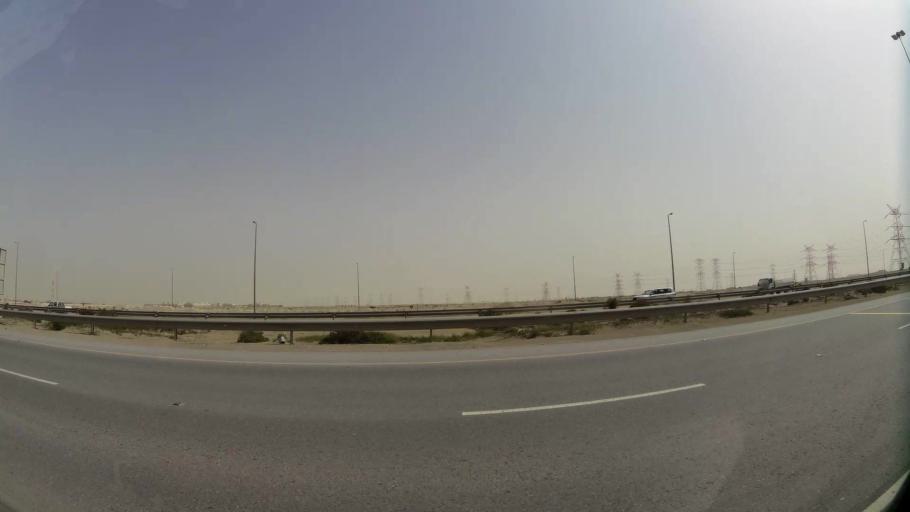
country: QA
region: Baladiyat ar Rayyan
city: Ar Rayyan
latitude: 25.1764
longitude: 51.3371
